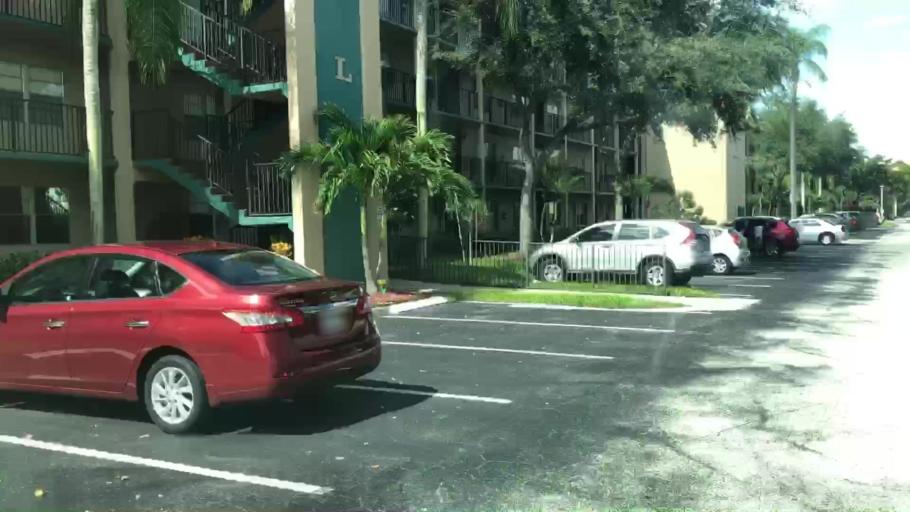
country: US
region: Florida
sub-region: Broward County
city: Sunshine Ranches
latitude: 26.0030
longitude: -80.3144
